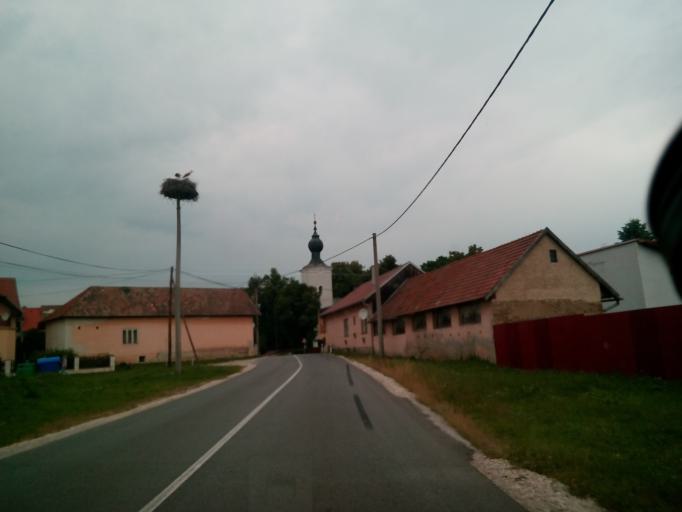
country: SK
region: Kosicky
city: Spisska Nova Ves
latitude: 48.9298
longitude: 20.6333
